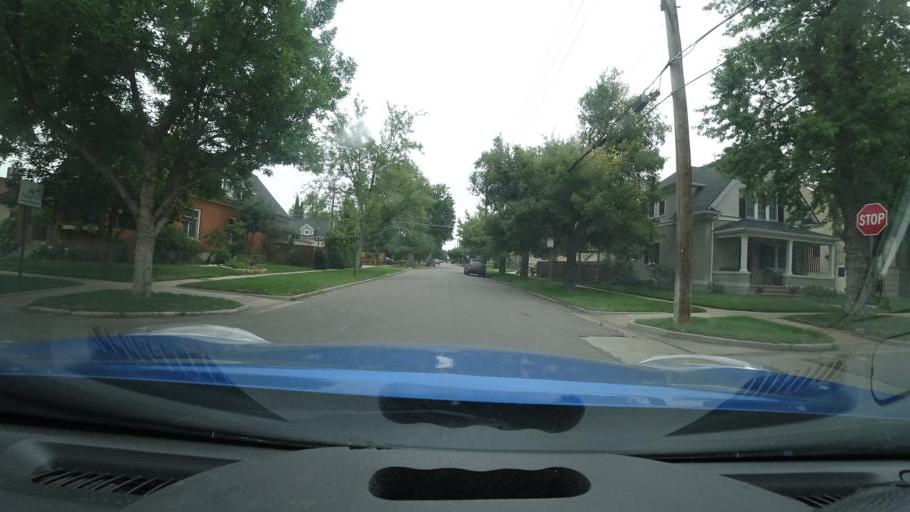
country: US
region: Colorado
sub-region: Arapahoe County
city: Englewood
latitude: 39.6840
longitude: -104.9771
